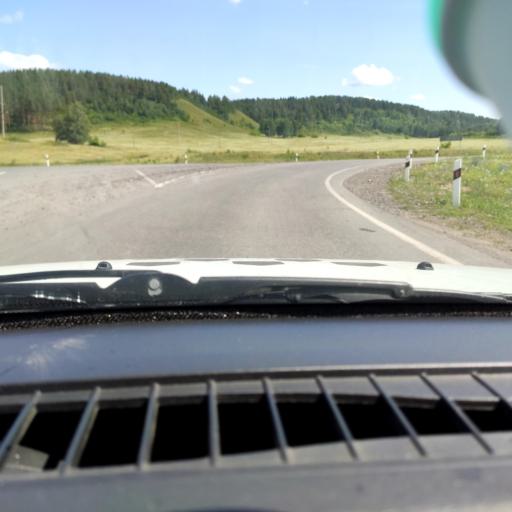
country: RU
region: Bashkortostan
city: Mesyagutovo
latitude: 55.5209
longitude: 58.2916
